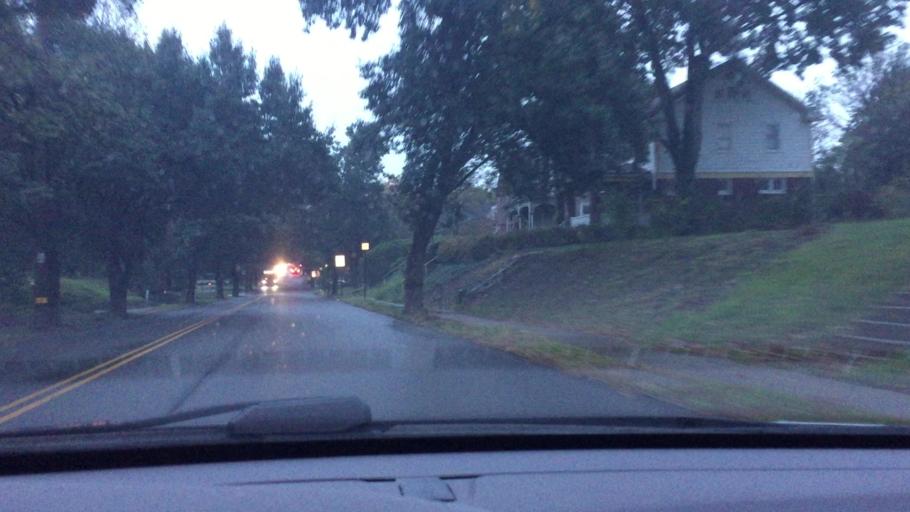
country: US
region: Pennsylvania
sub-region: Allegheny County
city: Ingram
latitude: 40.4398
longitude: -80.0776
